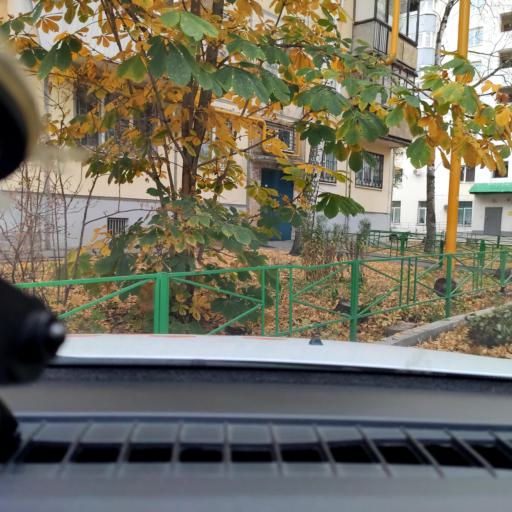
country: RU
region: Samara
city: Samara
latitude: 53.1988
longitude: 50.1703
